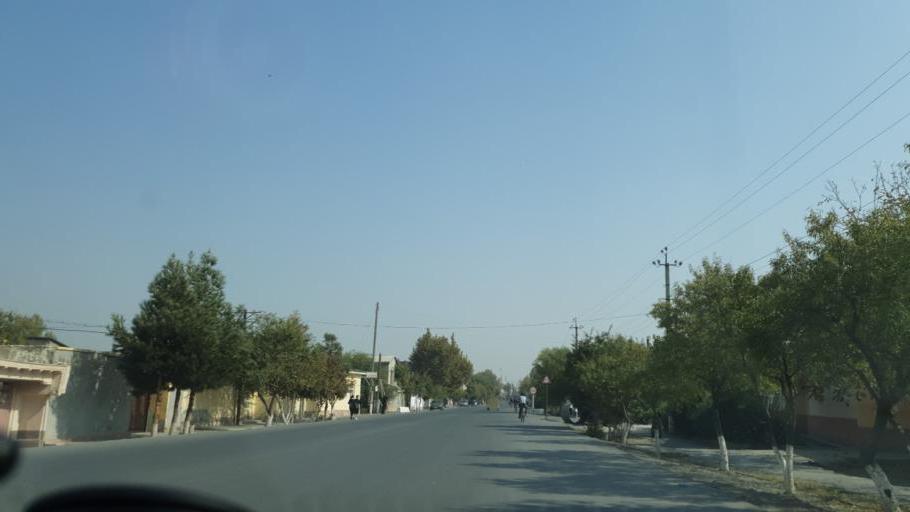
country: UZ
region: Fergana
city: Beshariq
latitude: 40.4360
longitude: 70.5970
